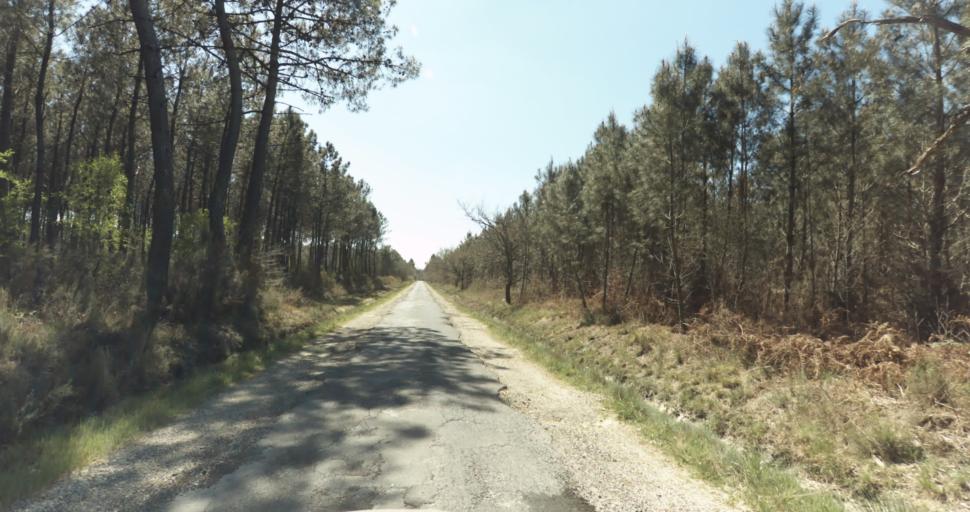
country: FR
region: Aquitaine
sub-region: Departement de la Gironde
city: Martignas-sur-Jalle
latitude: 44.7940
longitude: -0.7556
